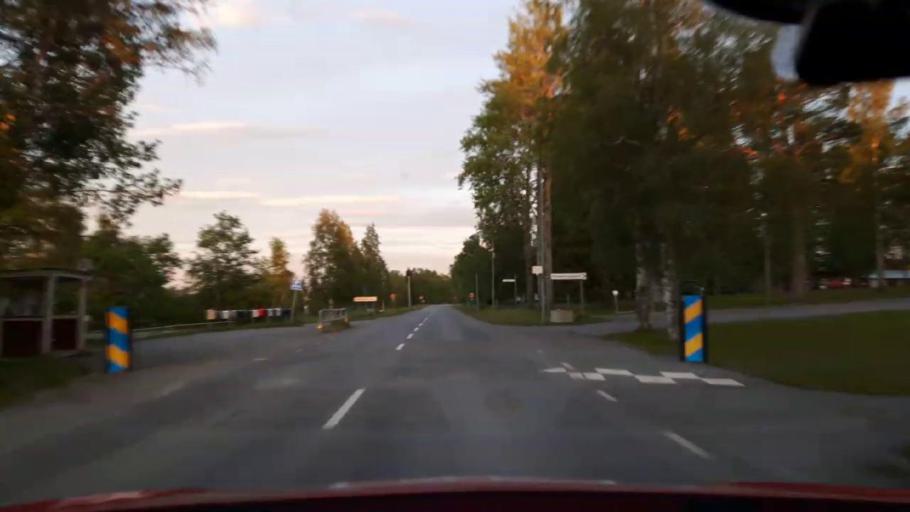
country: SE
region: Jaemtland
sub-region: OEstersunds Kommun
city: Brunflo
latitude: 63.1110
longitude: 14.7319
